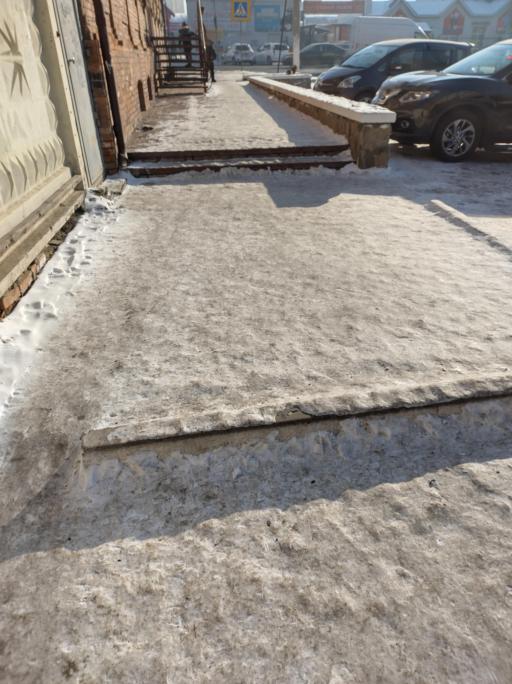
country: RU
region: Transbaikal Territory
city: Chita
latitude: 52.0396
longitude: 113.4930
